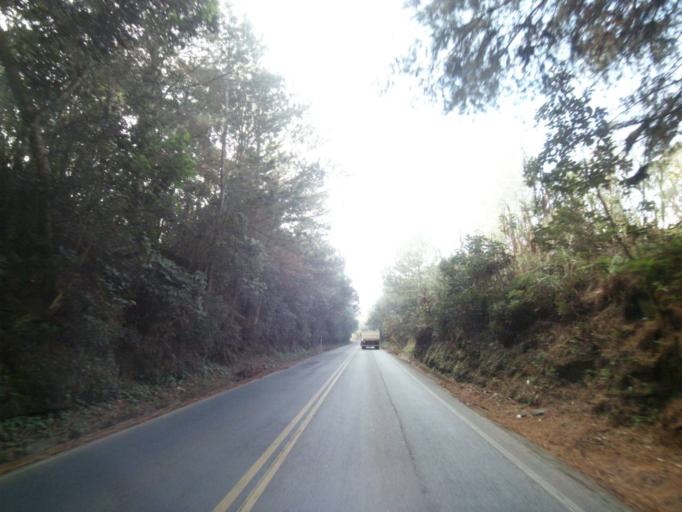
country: BR
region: Parana
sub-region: Tibagi
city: Tibagi
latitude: -24.5280
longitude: -50.3912
